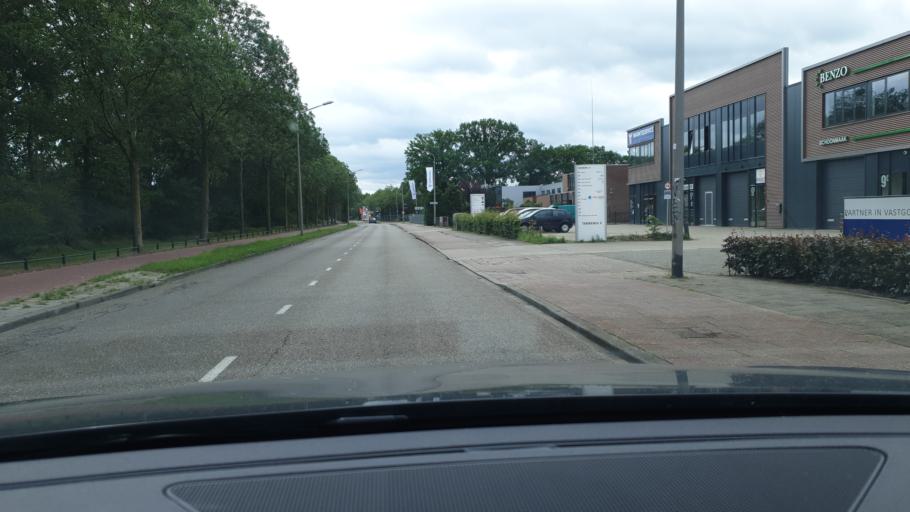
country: NL
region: Gelderland
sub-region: Gemeente Nijmegen
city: Lindenholt
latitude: 51.8197
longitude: 5.8219
